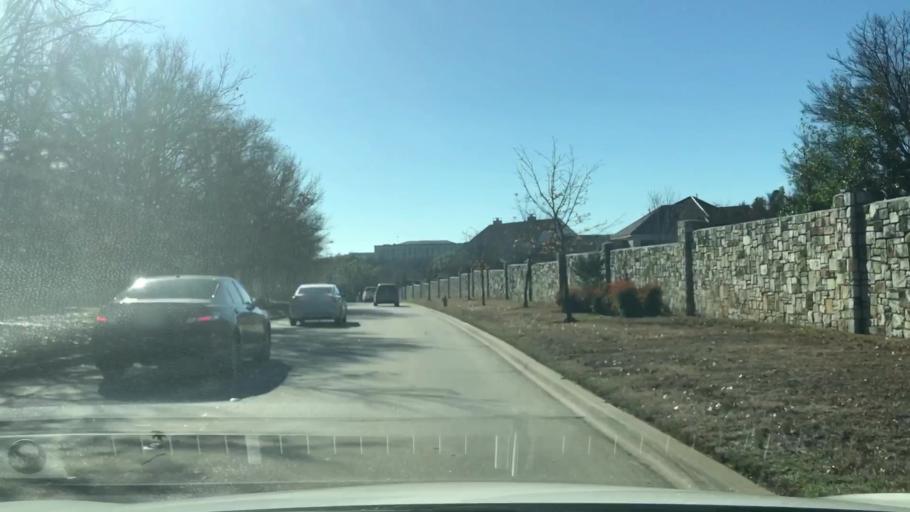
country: US
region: Texas
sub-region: Denton County
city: The Colony
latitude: 33.0977
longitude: -96.8420
